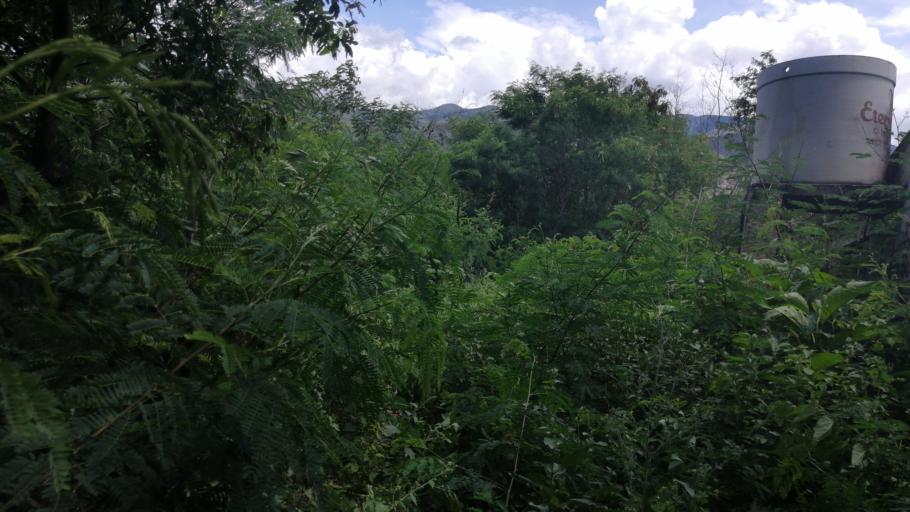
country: CO
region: Boyaca
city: Soata
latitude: 6.2864
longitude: -72.6497
